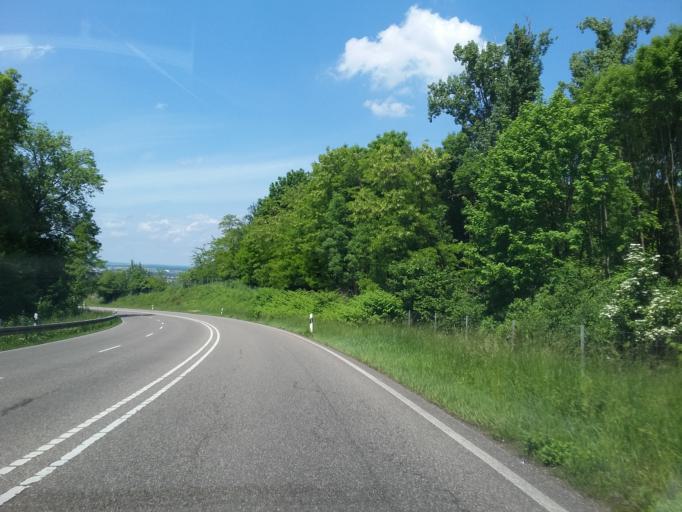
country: DE
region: Baden-Wuerttemberg
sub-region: Regierungsbezirk Stuttgart
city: Flein
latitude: 49.1117
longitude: 9.2330
